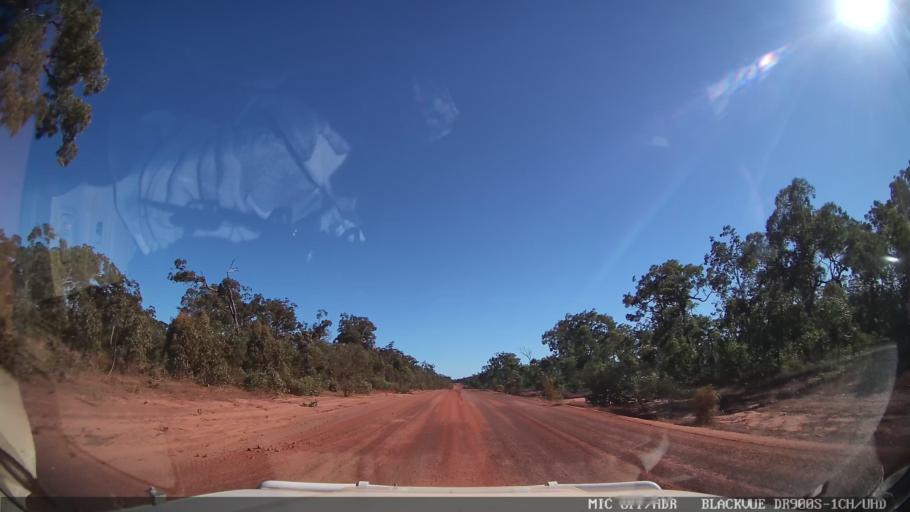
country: AU
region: Queensland
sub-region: Torres
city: Thursday Island
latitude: -11.3957
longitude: 142.3566
